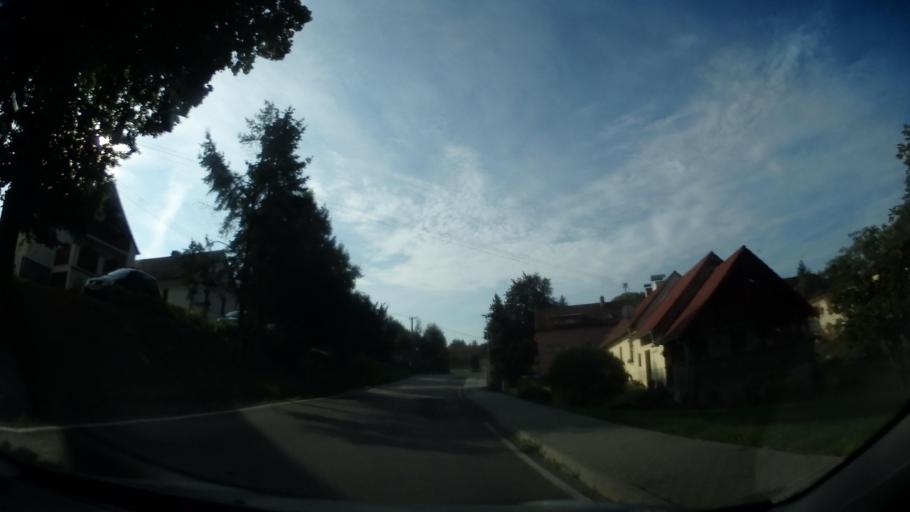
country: CZ
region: Jihocesky
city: Cimelice
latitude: 49.4176
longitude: 14.1170
